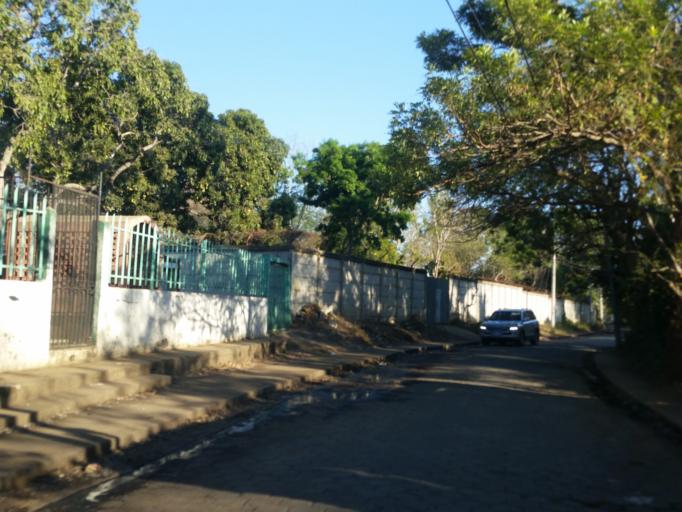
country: NI
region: Masaya
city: Ticuantepe
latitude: 12.0722
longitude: -86.2143
